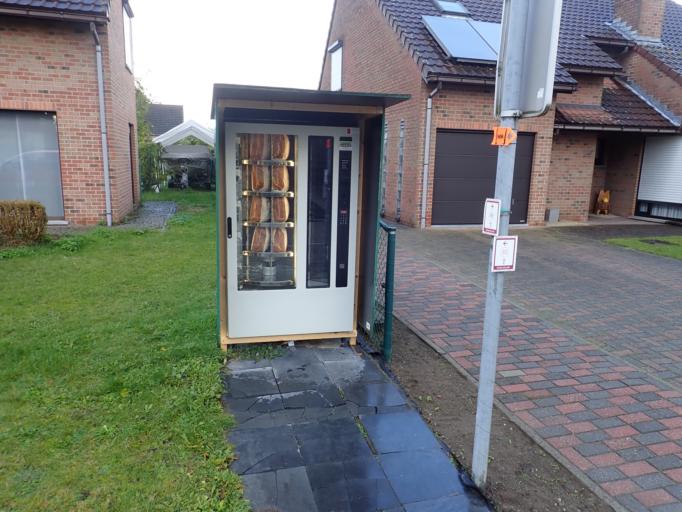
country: BE
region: Flanders
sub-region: Provincie Antwerpen
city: Niel
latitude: 51.0902
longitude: 4.3252
